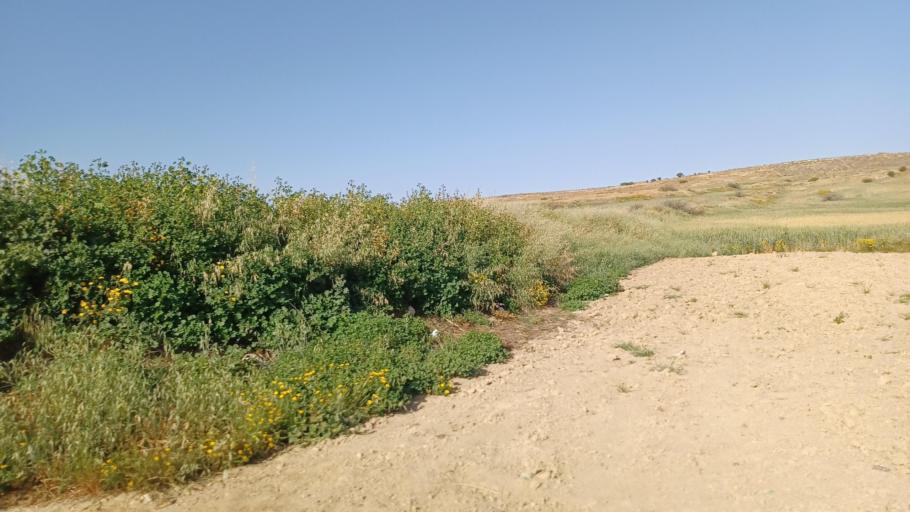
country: CY
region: Lefkosia
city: Mammari
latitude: 35.1597
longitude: 33.2427
